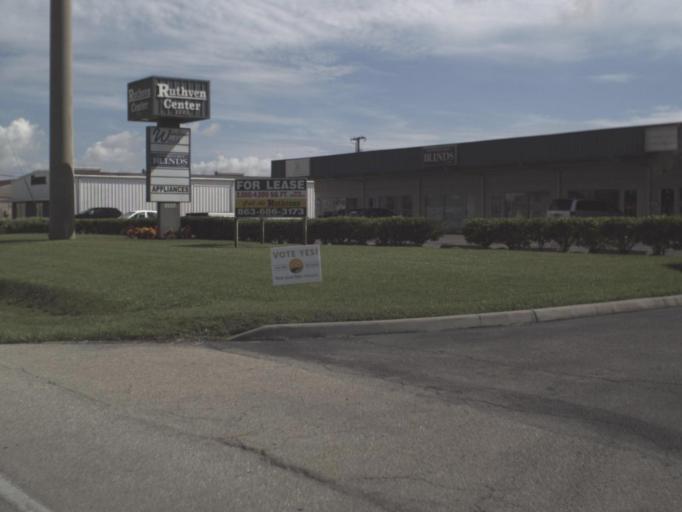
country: US
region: Florida
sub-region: Polk County
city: Crystal Lake
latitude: 28.0165
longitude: -81.9078
